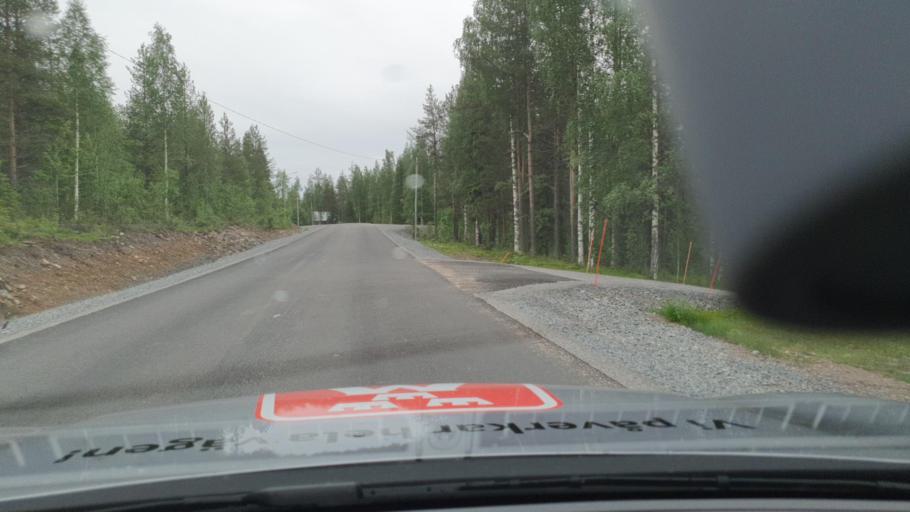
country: SE
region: Norrbotten
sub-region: Overtornea Kommun
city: OEvertornea
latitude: 66.5983
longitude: 23.3070
